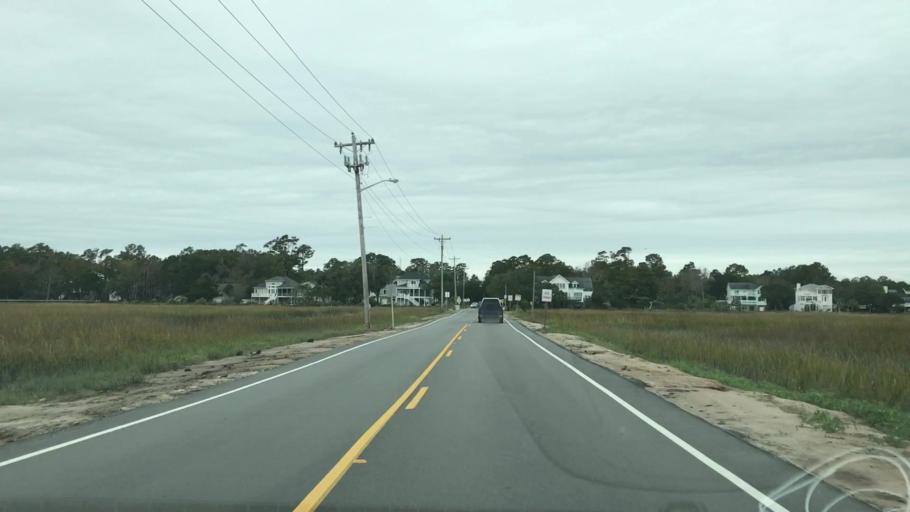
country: US
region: South Carolina
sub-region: Horry County
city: Garden City
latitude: 33.5825
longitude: -78.9970
